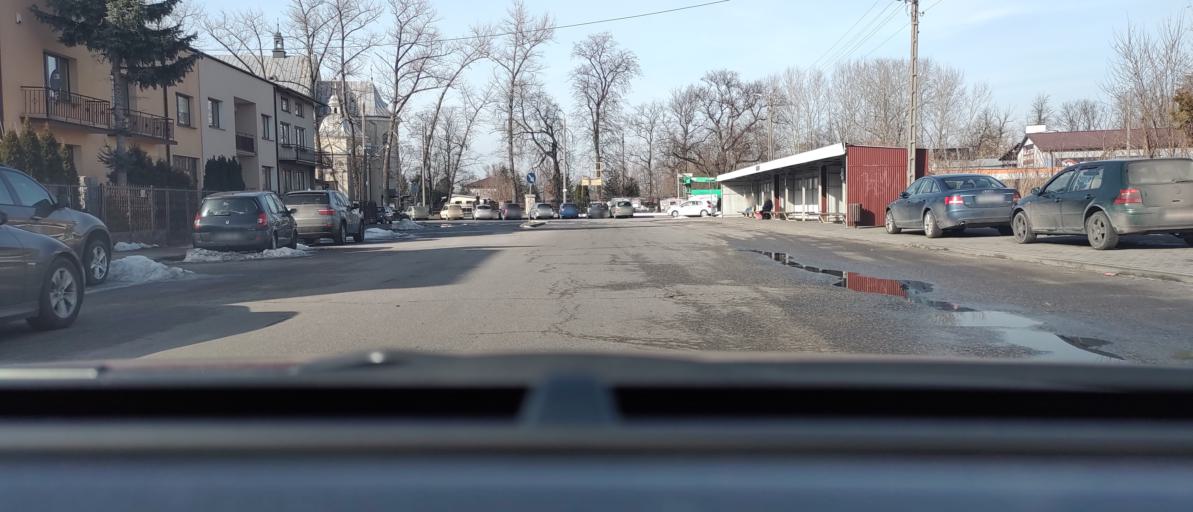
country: PL
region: Masovian Voivodeship
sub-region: Powiat bialobrzeski
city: Bialobrzegi
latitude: 51.6501
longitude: 20.9556
